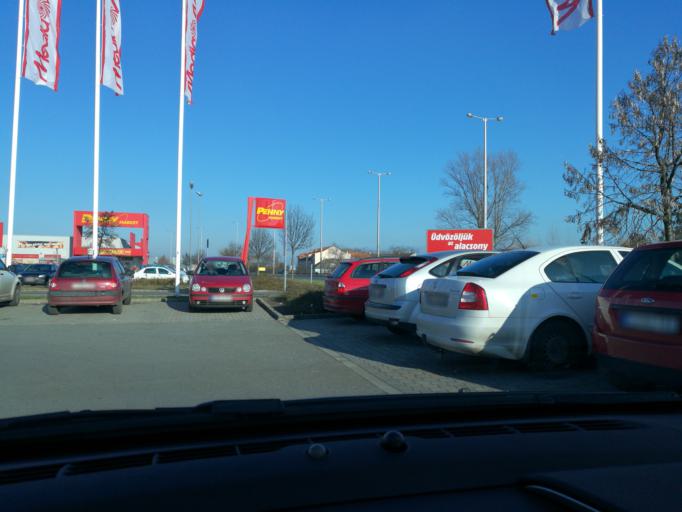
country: HU
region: Szabolcs-Szatmar-Bereg
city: Nyiregyhaza
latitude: 47.9576
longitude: 21.7284
